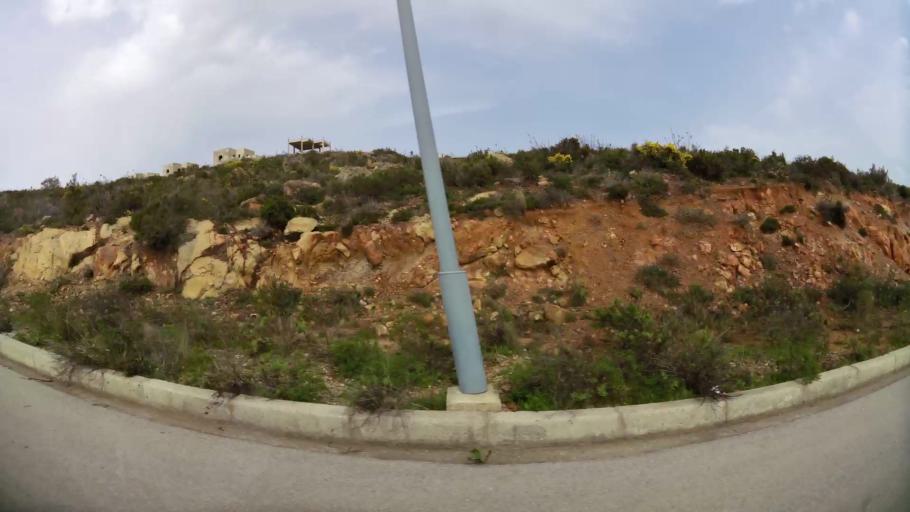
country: MA
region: Tanger-Tetouan
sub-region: Tanger-Assilah
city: Boukhalef
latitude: 35.6979
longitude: -5.9415
